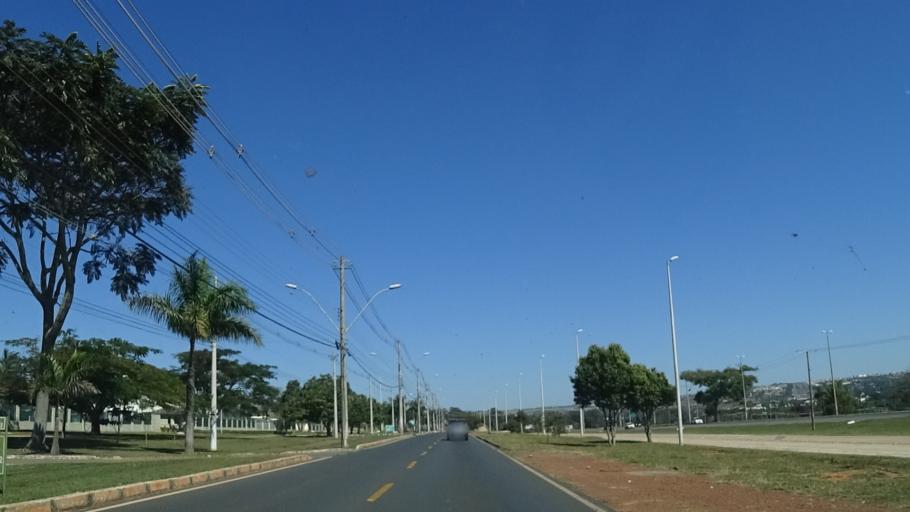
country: BR
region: Federal District
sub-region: Brasilia
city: Brasilia
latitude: -15.8733
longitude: -47.9533
